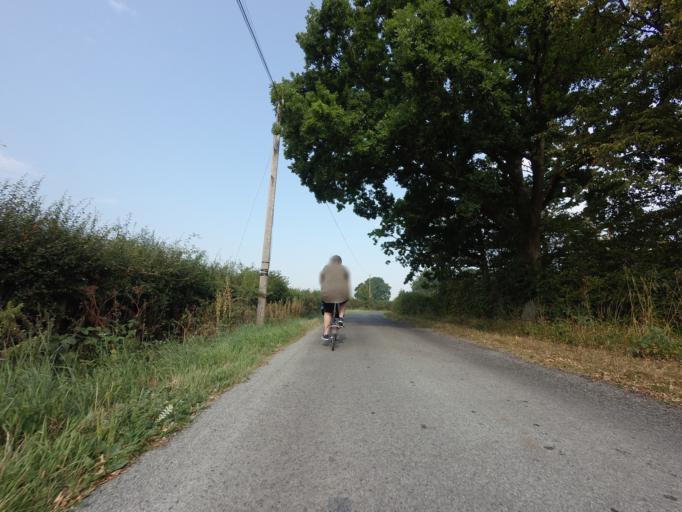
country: GB
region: England
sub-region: Kent
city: Headcorn
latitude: 51.1244
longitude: 0.6637
